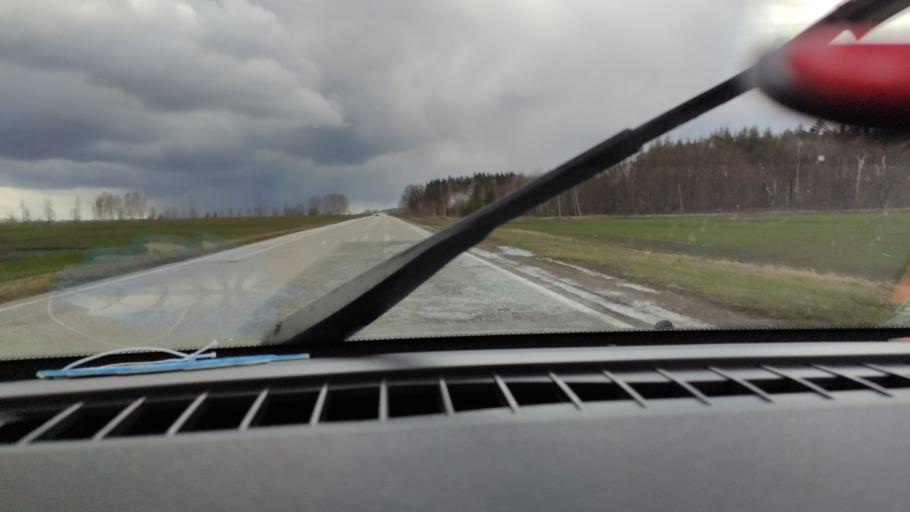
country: RU
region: Samara
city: Povolzhskiy
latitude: 53.8029
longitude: 49.7837
